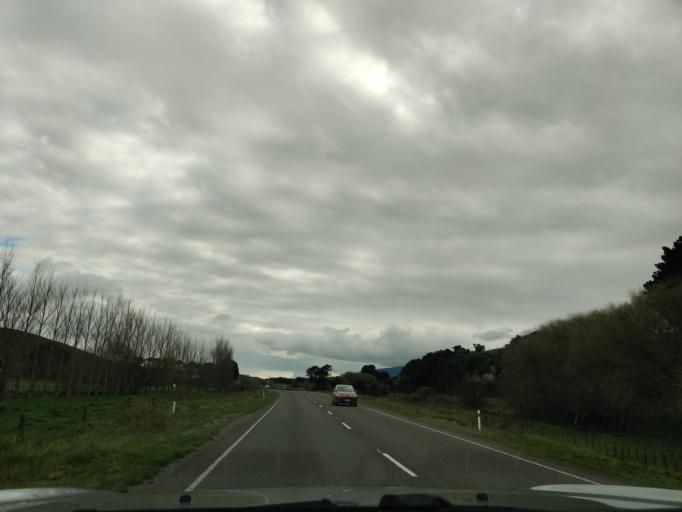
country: NZ
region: Manawatu-Wanganui
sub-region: Palmerston North City
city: Palmerston North
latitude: -40.2818
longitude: 175.9903
